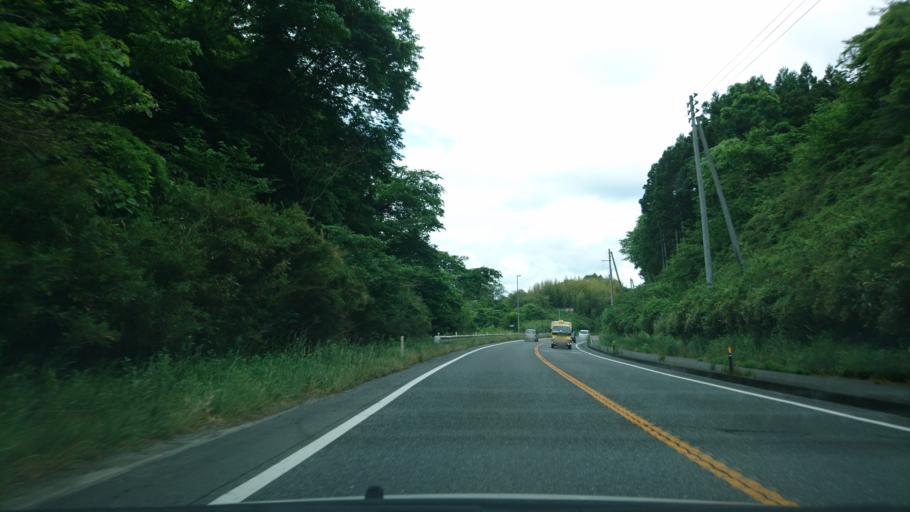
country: JP
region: Iwate
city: Ichinoseki
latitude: 38.9088
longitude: 141.1112
